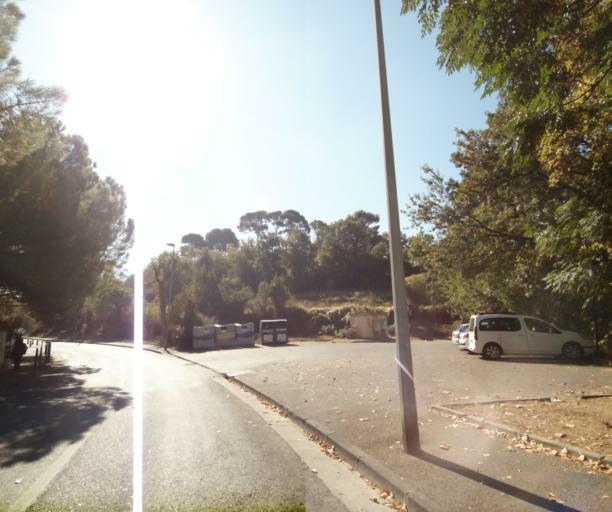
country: FR
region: Provence-Alpes-Cote d'Azur
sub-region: Departement des Bouches-du-Rhone
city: Plan-de-Cuques
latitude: 43.3424
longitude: 5.4641
